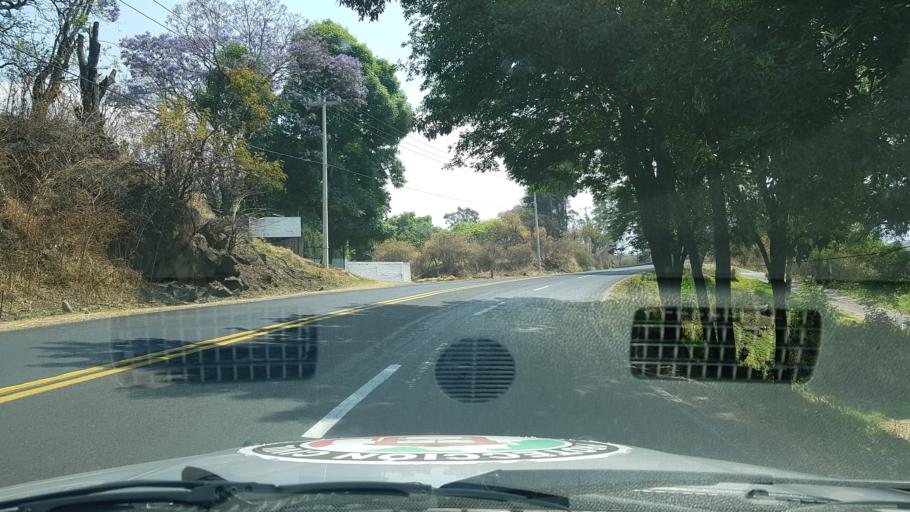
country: MX
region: Mexico
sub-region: Tepetlixpa
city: Nepantla de Sor Juana Ines de la Cruz
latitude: 18.9900
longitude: -98.8276
